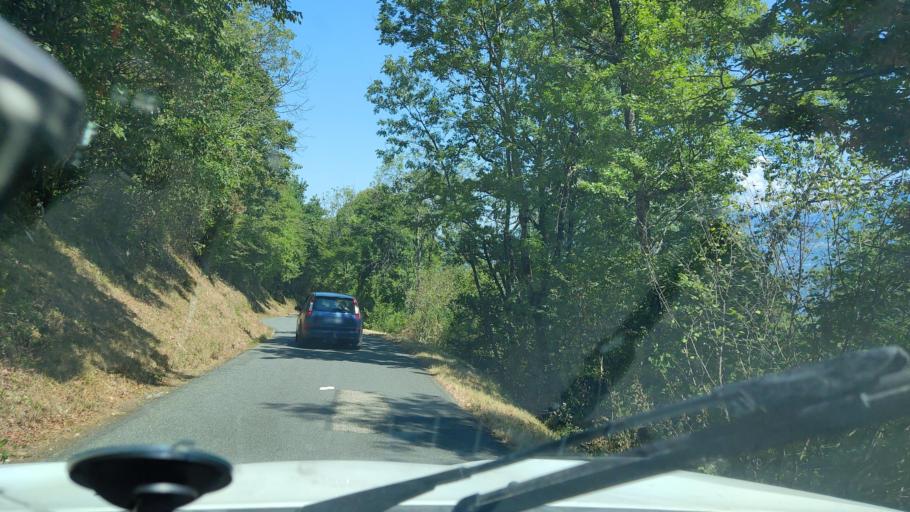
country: FR
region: Rhone-Alpes
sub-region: Departement de la Savoie
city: Le Bourget-du-Lac
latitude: 45.6522
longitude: 5.8388
